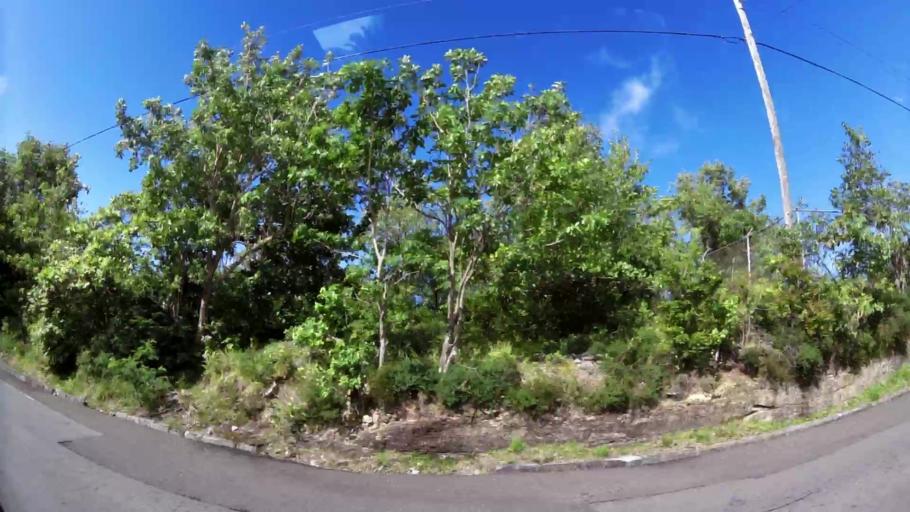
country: LC
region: Choiseul Quarter
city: Choiseul
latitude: 13.7952
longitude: -61.0385
